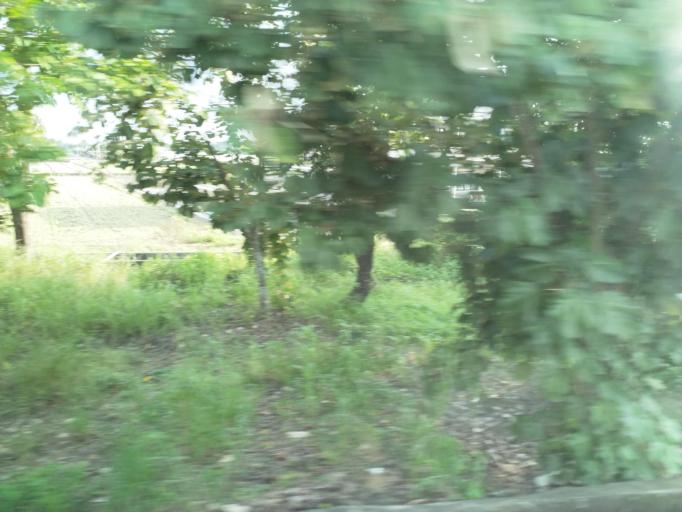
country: TW
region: Taiwan
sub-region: Pingtung
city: Pingtung
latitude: 22.8862
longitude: 120.5158
